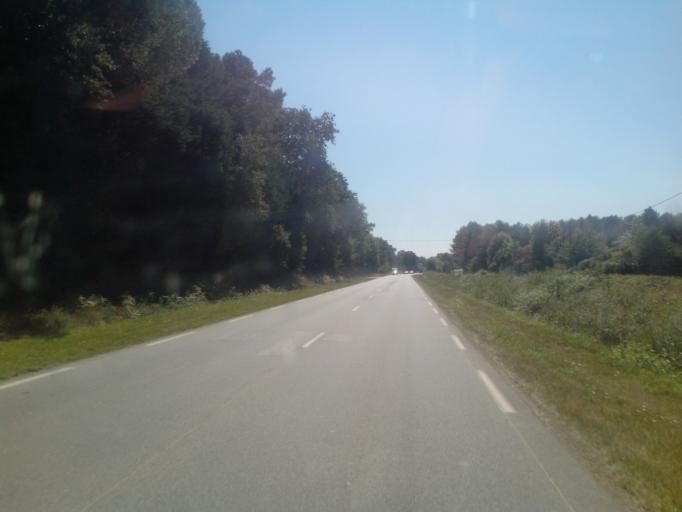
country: FR
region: Brittany
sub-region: Departement du Morbihan
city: Molac
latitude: 47.7397
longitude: -2.4380
